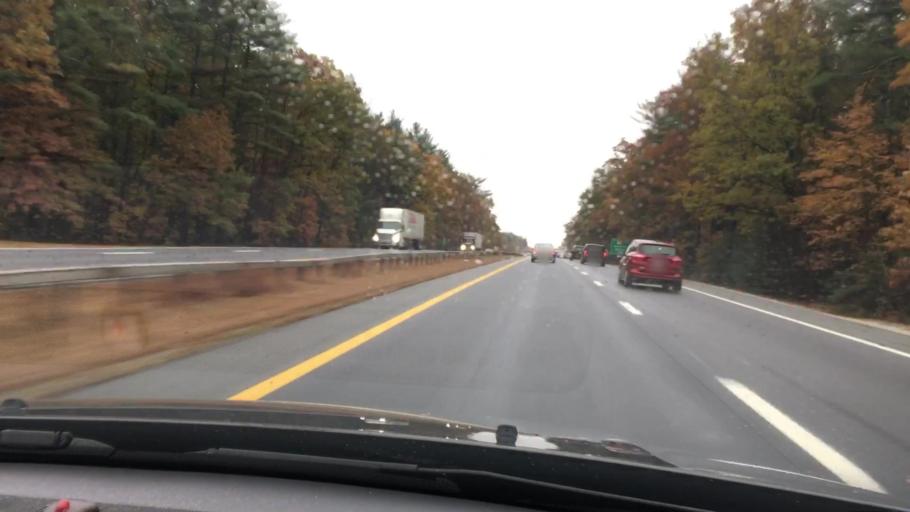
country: US
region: New Hampshire
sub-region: Hillsborough County
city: Litchfield
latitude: 42.8012
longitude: -71.4982
